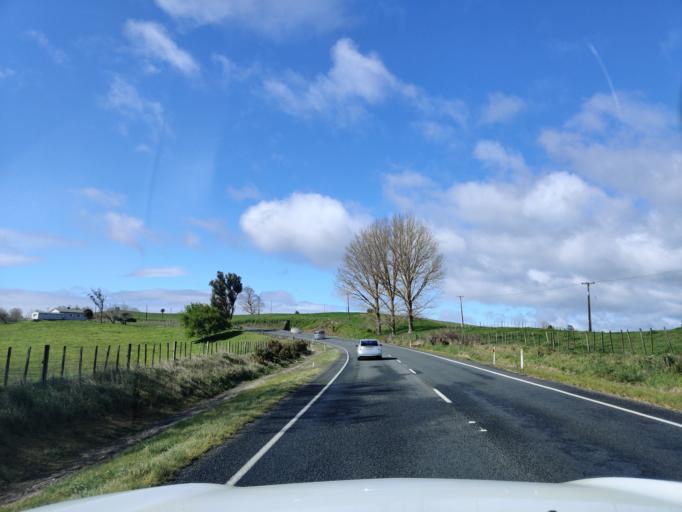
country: NZ
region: Waikato
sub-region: Otorohanga District
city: Otorohanga
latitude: -38.0930
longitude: 175.1826
